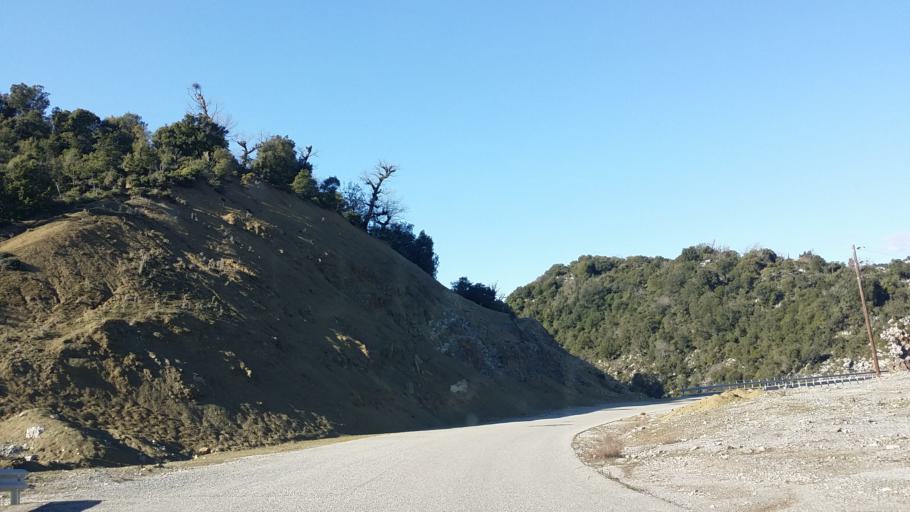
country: GR
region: Central Greece
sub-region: Nomos Evrytanias
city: Kerasochori
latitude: 38.9650
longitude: 21.4596
